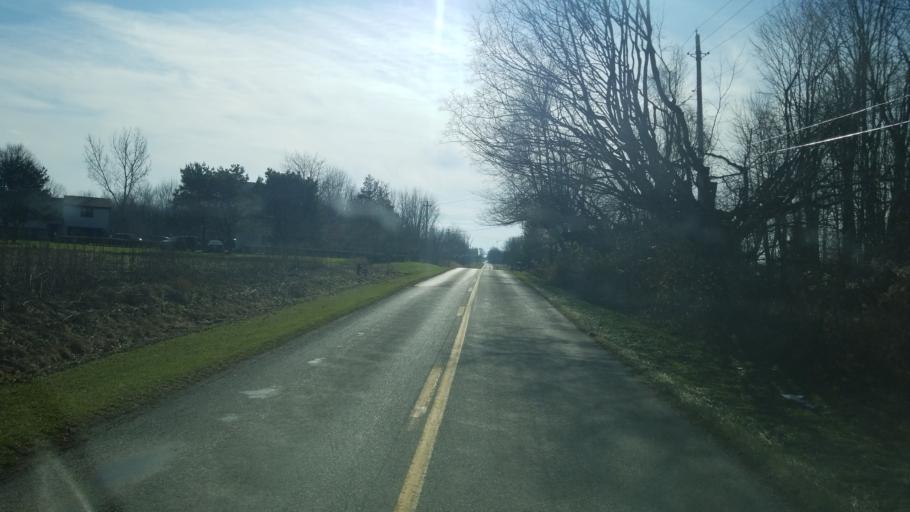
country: US
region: Ohio
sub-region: Ashtabula County
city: Roaming Shores
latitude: 41.6995
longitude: -80.8359
